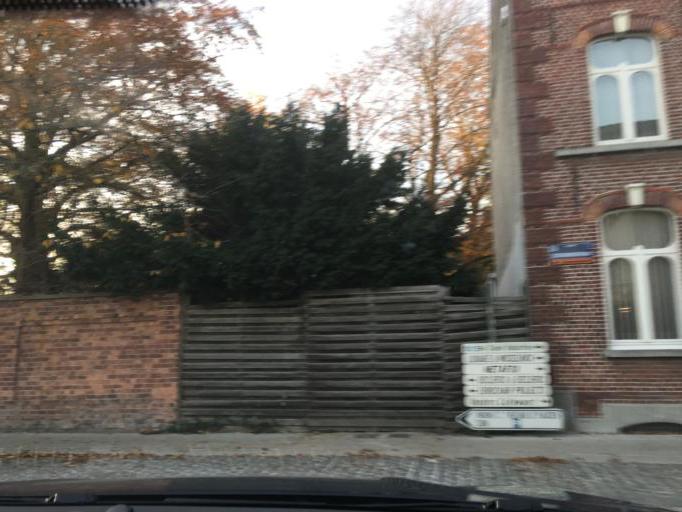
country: BE
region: Flanders
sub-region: Provincie West-Vlaanderen
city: Ardooie
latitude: 50.9815
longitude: 3.2004
